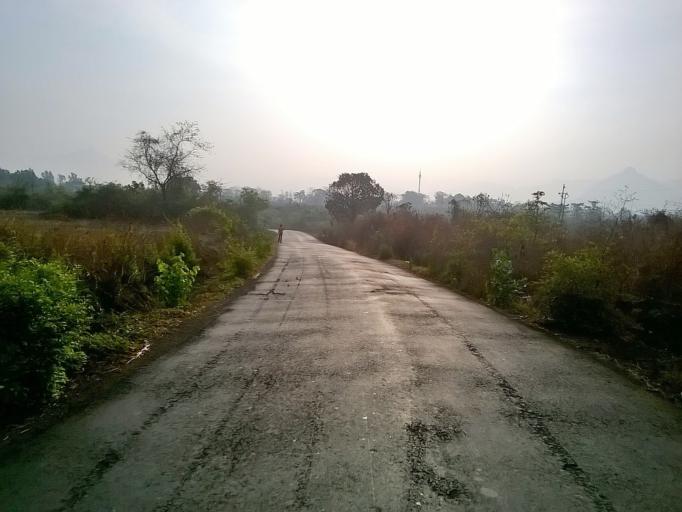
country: IN
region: Maharashtra
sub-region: Raigarh
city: Kalundri
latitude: 19.0180
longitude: 73.1817
